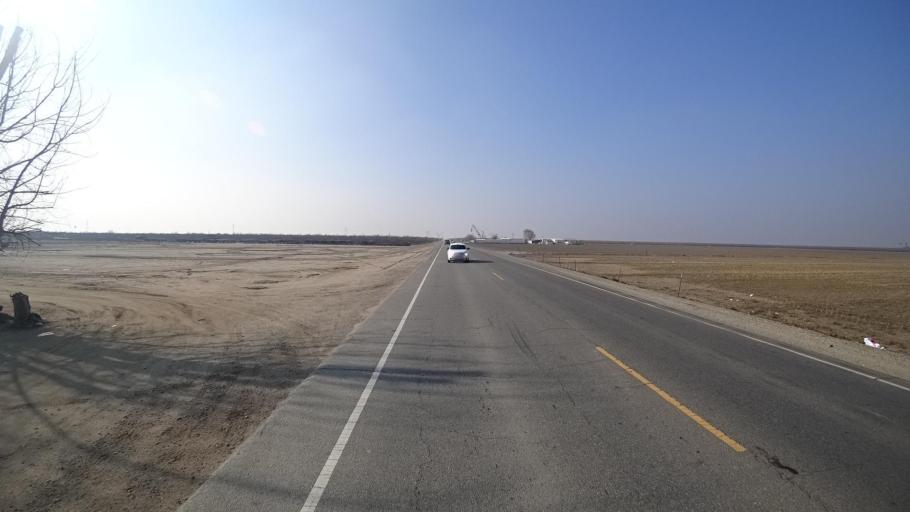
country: US
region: California
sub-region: Kern County
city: Greenacres
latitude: 35.2672
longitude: -119.1224
